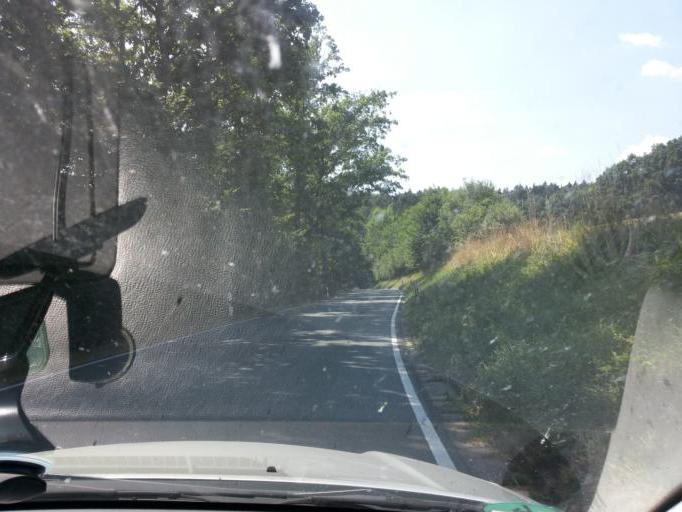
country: DE
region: Bavaria
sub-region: Regierungsbezirk Mittelfranken
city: Markt Erlbach
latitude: 49.5069
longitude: 10.6813
